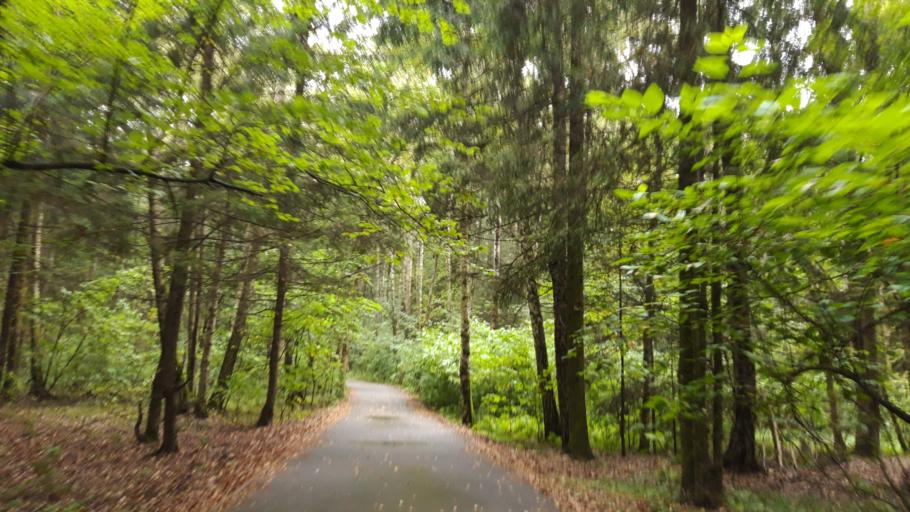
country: RU
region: Moscow
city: Zelenograd
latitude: 55.9848
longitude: 37.2045
